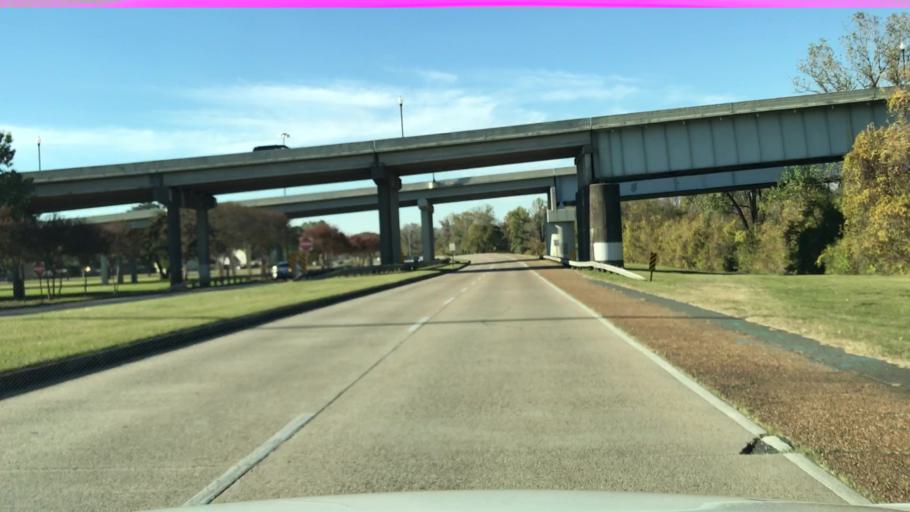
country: US
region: Louisiana
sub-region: Bossier Parish
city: Bossier City
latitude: 32.4903
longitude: -93.7002
